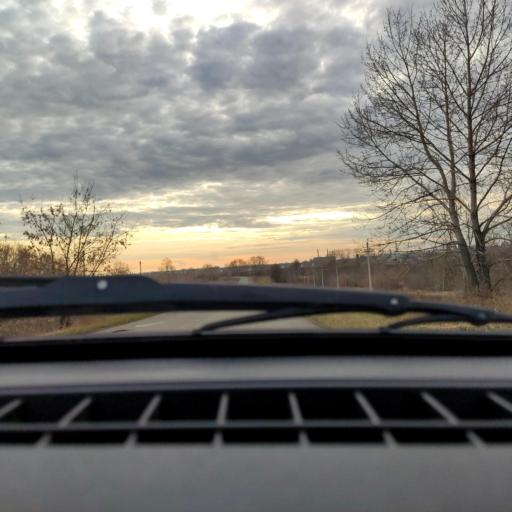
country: RU
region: Bashkortostan
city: Blagoveshchensk
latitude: 54.8875
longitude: 56.1422
